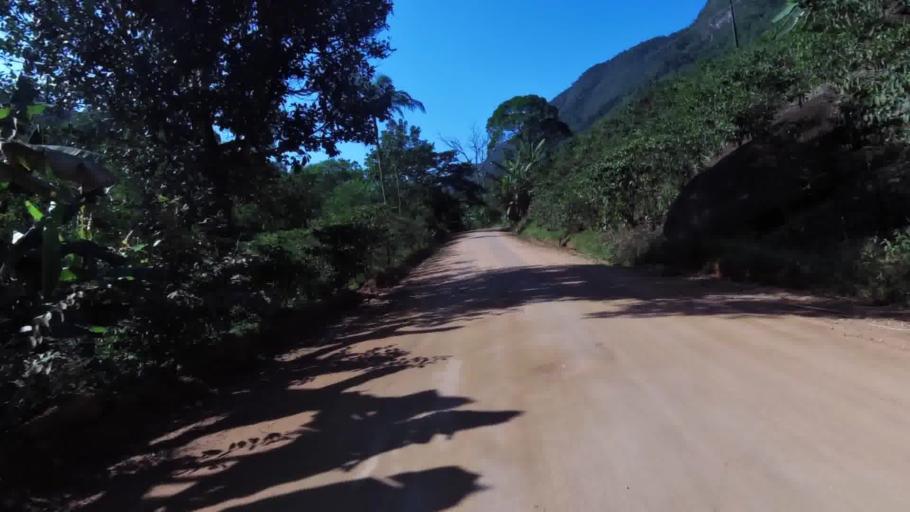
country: BR
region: Espirito Santo
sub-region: Alfredo Chaves
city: Alfredo Chaves
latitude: -20.5571
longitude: -40.7294
